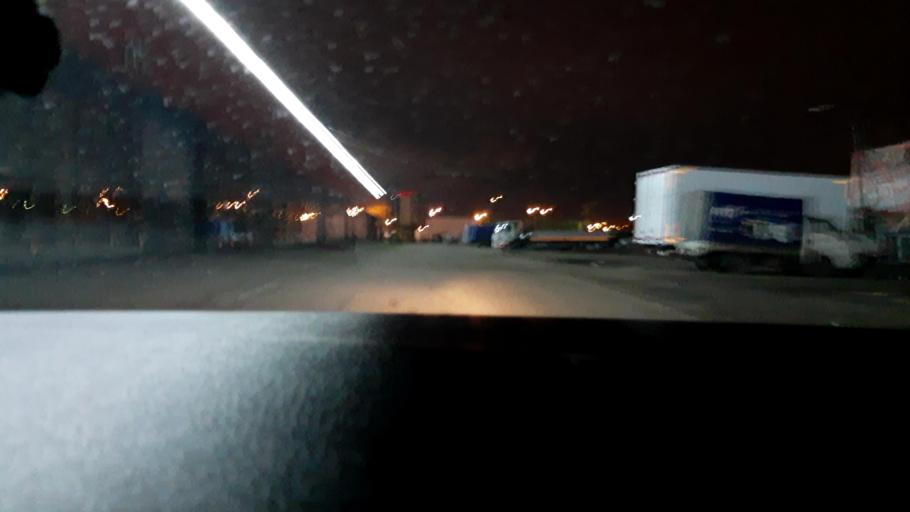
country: RU
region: Moscow
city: Annino
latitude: 55.5790
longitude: 37.5908
